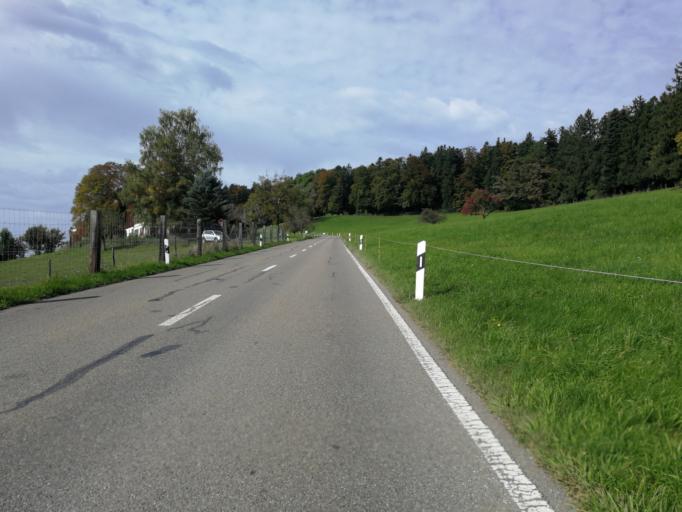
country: CH
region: Zurich
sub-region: Bezirk Meilen
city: Uetikon / Grossdorf
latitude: 47.2801
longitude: 8.6880
